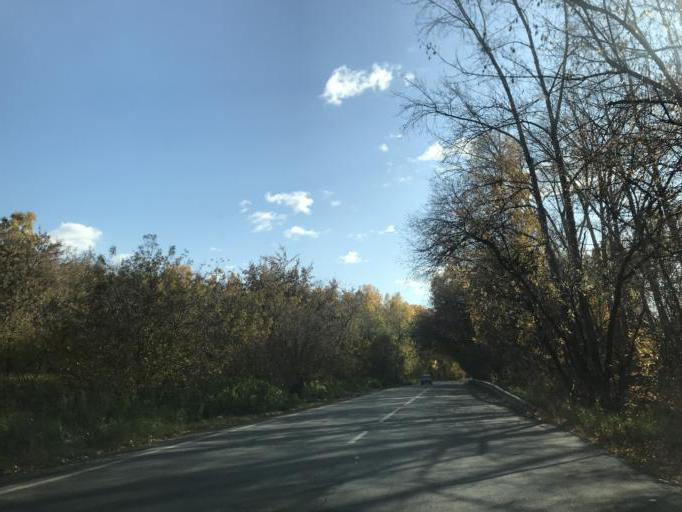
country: RU
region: Chelyabinsk
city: Dolgoderevenskoye
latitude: 55.2641
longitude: 61.3645
